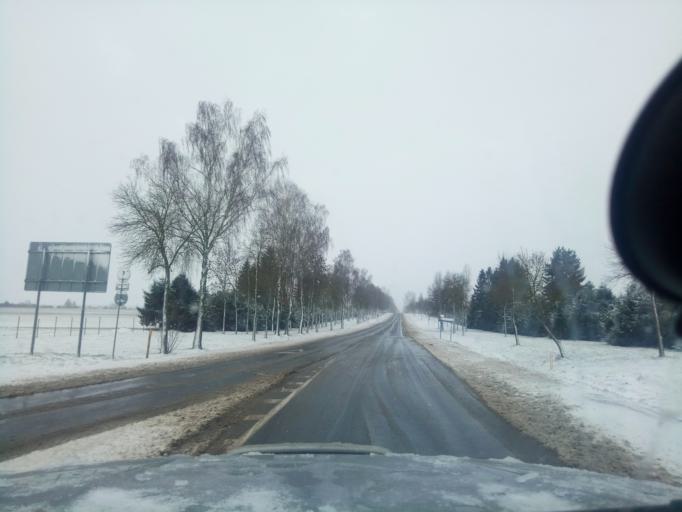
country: BY
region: Minsk
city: Haradzyeya
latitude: 53.3594
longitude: 26.5144
